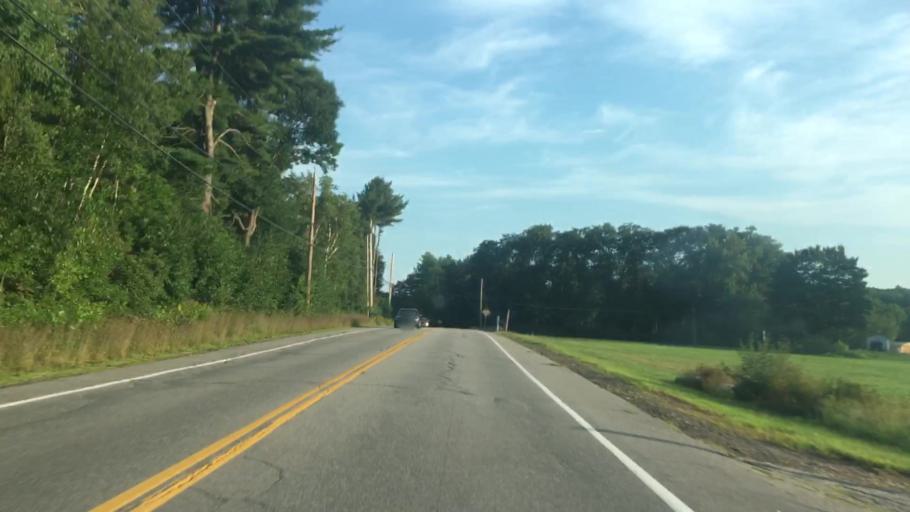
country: US
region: New Hampshire
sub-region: Belknap County
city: Gilmanton
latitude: 43.4369
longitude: -71.4172
